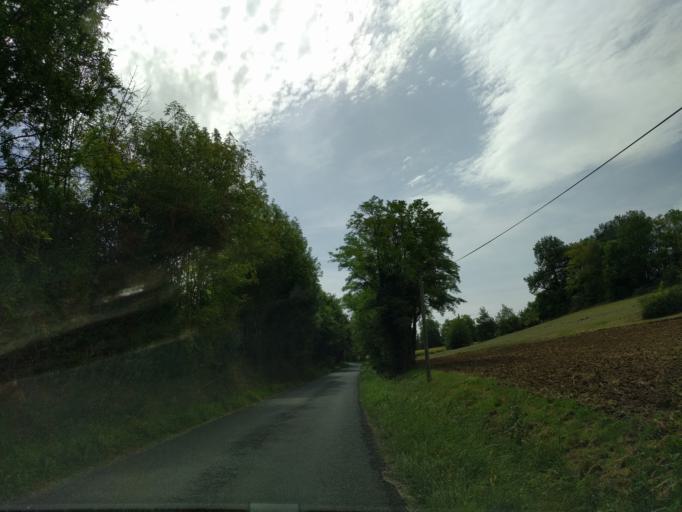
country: FR
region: Midi-Pyrenees
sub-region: Departement du Tarn
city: Castres
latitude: 43.6436
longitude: 2.2045
